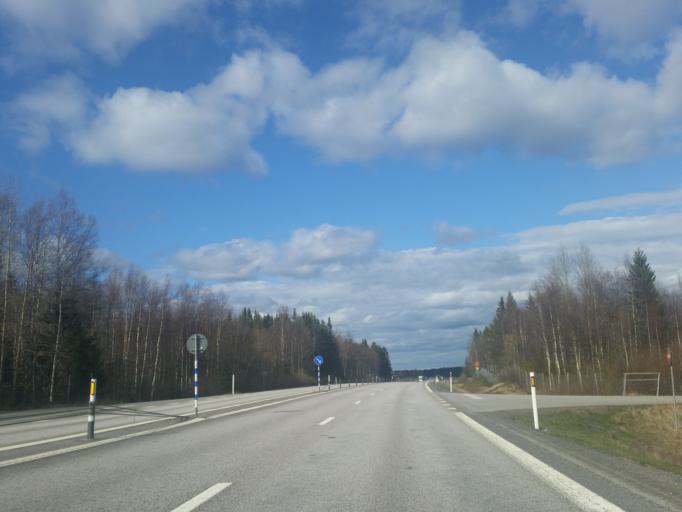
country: SE
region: Vaesterbotten
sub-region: Robertsfors Kommun
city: Robertsfors
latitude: 64.0670
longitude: 20.8513
